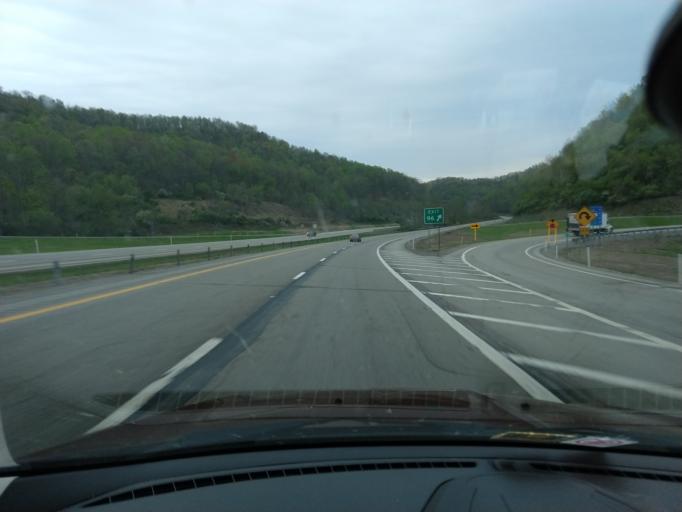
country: US
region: West Virginia
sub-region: Lewis County
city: Weston
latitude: 39.0144
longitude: -80.4696
